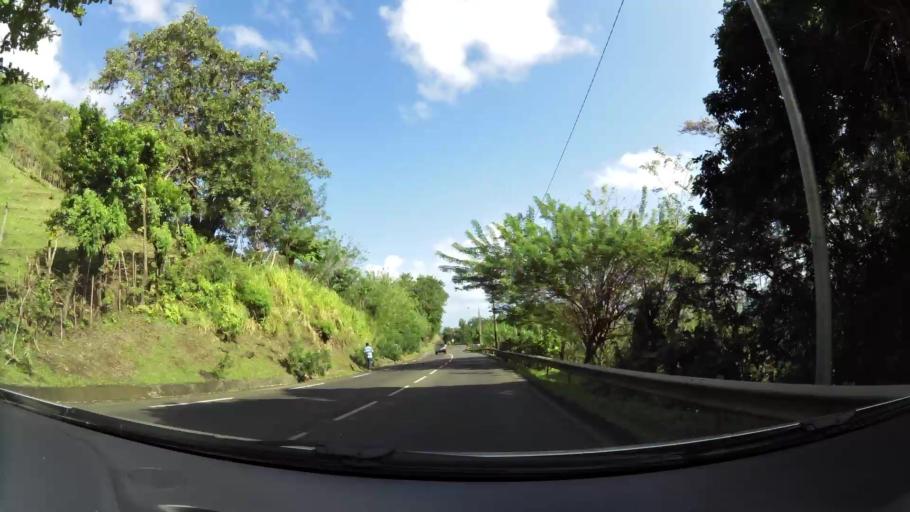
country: MQ
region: Martinique
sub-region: Martinique
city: Sainte-Marie
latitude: 14.7696
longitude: -60.9857
